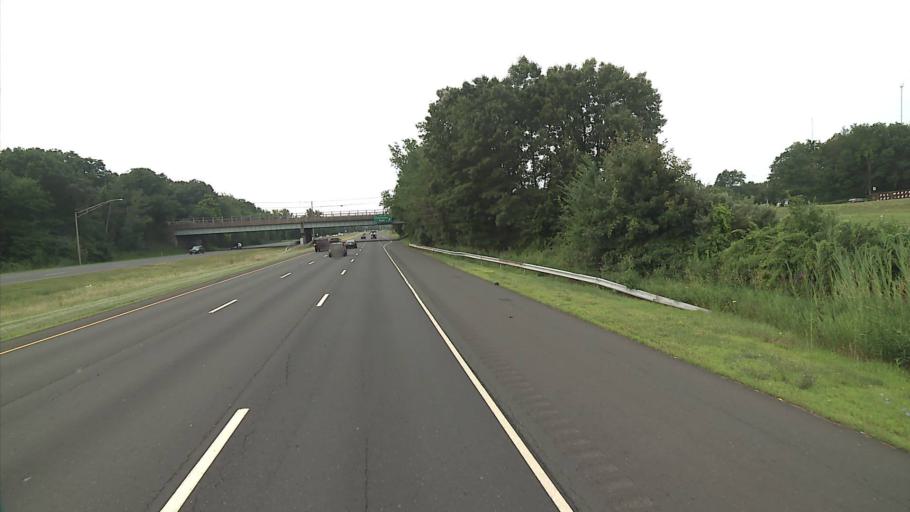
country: US
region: Connecticut
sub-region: Hartford County
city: Farmington
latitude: 41.7081
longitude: -72.8018
